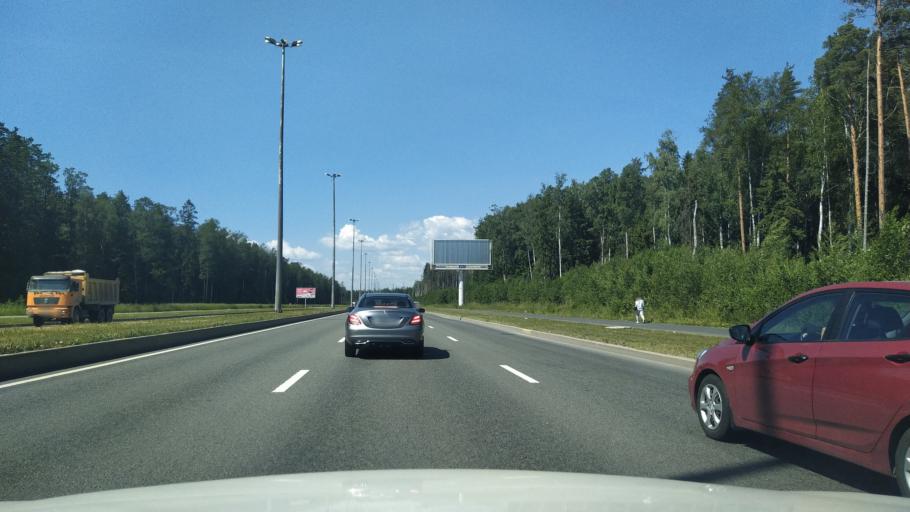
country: RU
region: Leningrad
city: Untolovo
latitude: 60.0562
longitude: 30.2232
